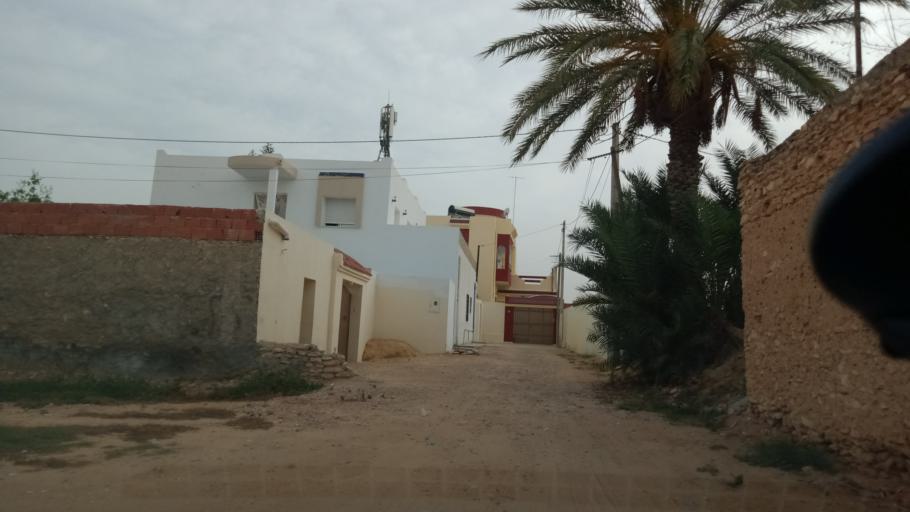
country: TN
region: Safaqis
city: Al Qarmadah
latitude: 34.7886
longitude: 10.7665
